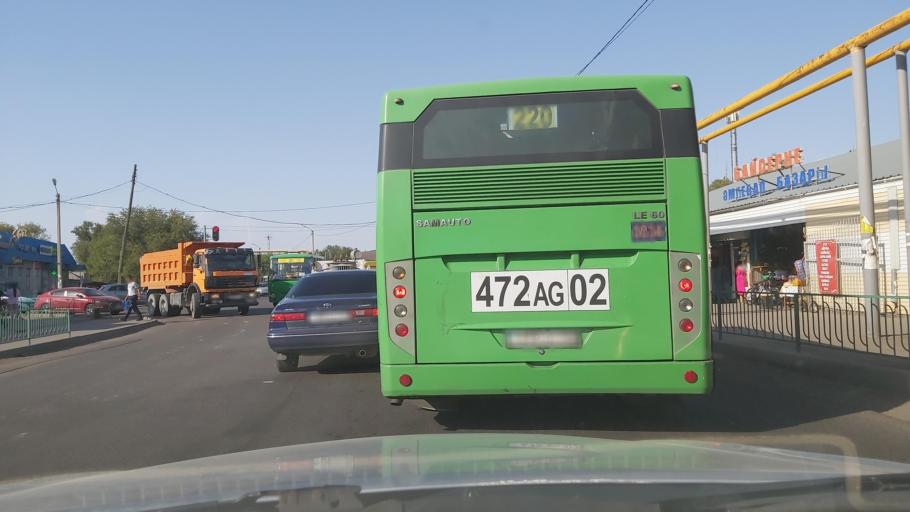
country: KZ
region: Almaty Oblysy
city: Energeticheskiy
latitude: 43.4834
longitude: 77.0342
